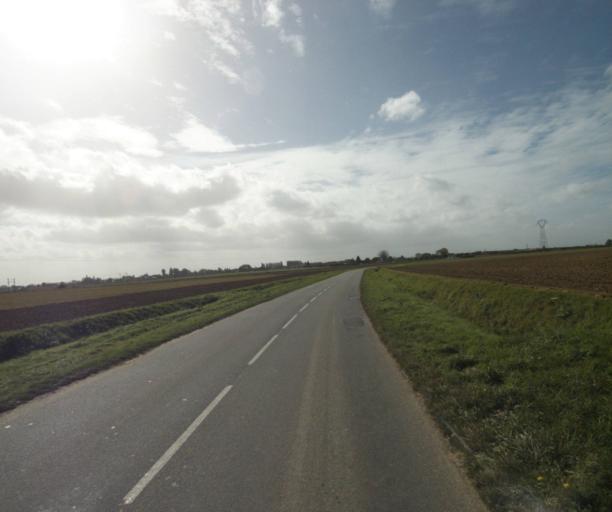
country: FR
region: Nord-Pas-de-Calais
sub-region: Departement du Nord
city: Salome
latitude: 50.5458
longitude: 2.8452
